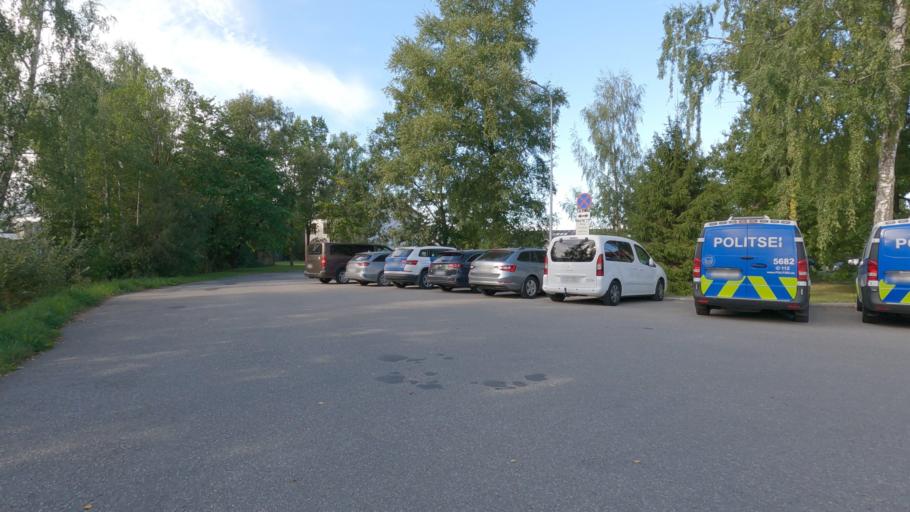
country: EE
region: Raplamaa
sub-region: Rapla vald
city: Rapla
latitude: 58.9945
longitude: 24.8256
